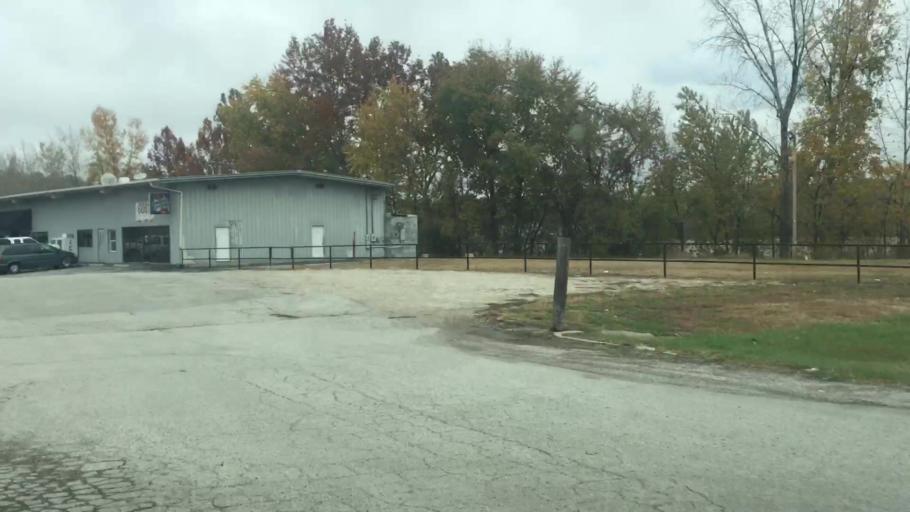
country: US
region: Missouri
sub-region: Gasconade County
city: Hermann
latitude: 38.7289
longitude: -91.4459
